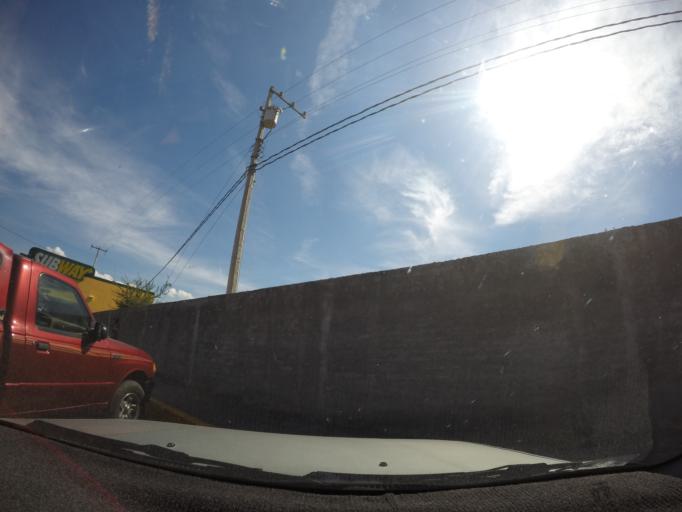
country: MX
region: Veracruz
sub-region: Papantla
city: Polutla
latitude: 20.4612
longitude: -97.2411
